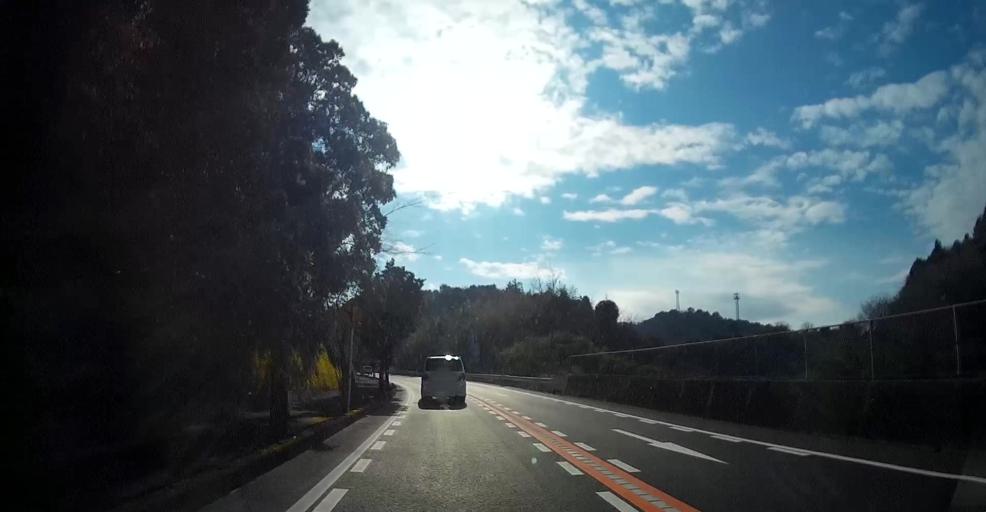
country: JP
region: Kumamoto
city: Yatsushiro
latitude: 32.6009
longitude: 130.4364
